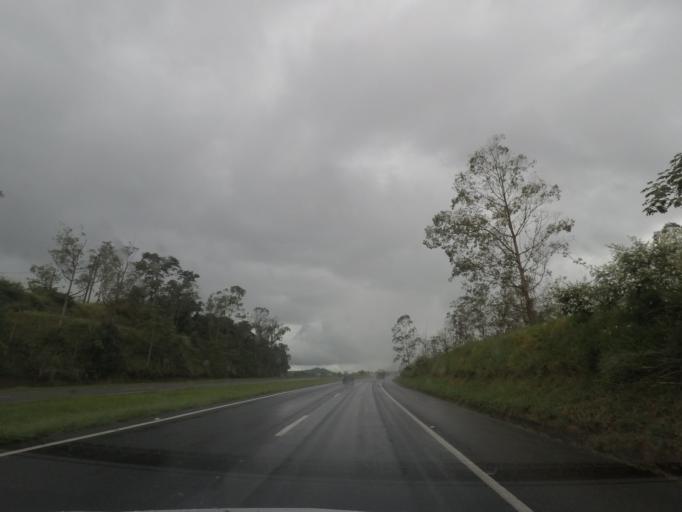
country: BR
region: Sao Paulo
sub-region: Juquia
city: Juquia
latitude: -24.3297
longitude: -47.5803
